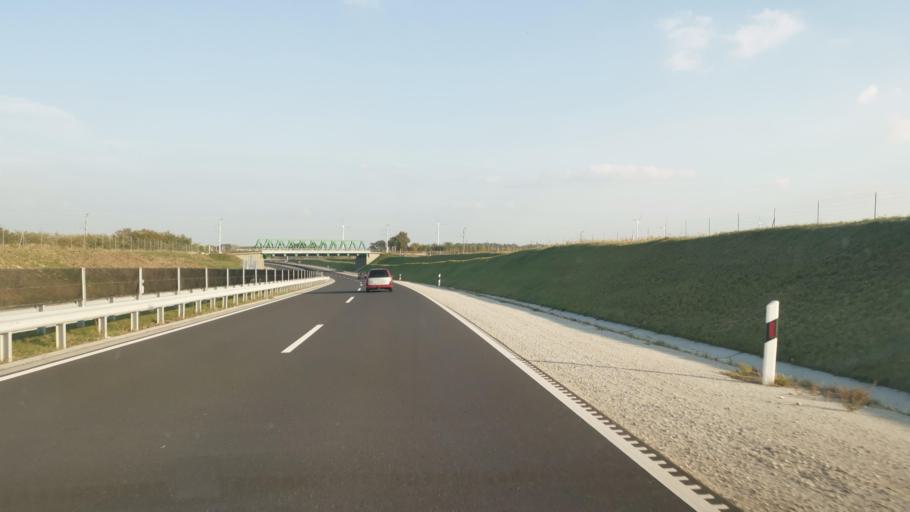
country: HU
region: Gyor-Moson-Sopron
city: Nagycenk
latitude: 47.5832
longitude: 16.7216
